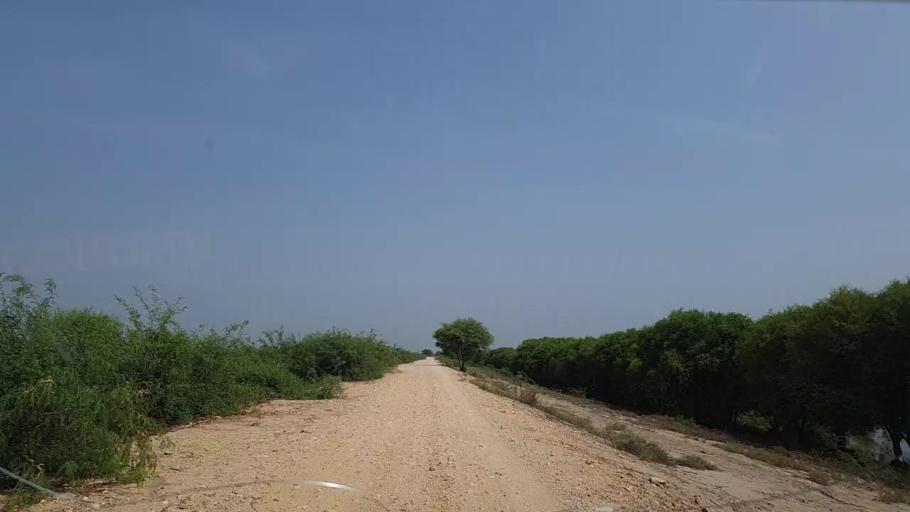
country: PK
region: Sindh
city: Ghotki
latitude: 28.0963
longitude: 69.4046
